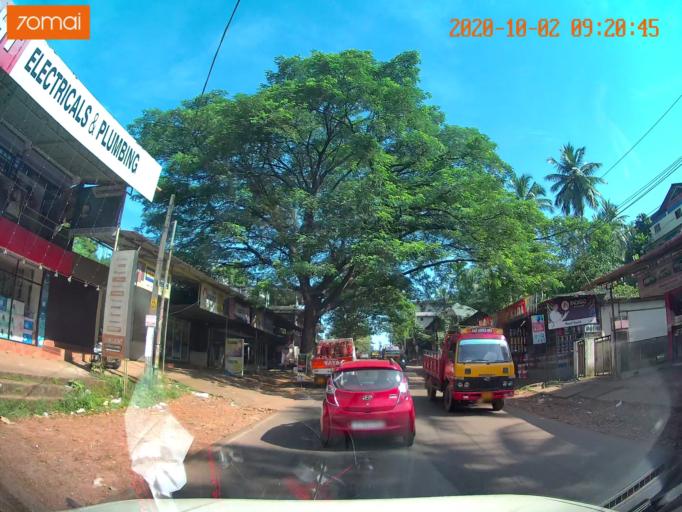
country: IN
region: Kerala
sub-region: Kozhikode
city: Naduvannur
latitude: 11.5695
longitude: 75.7537
